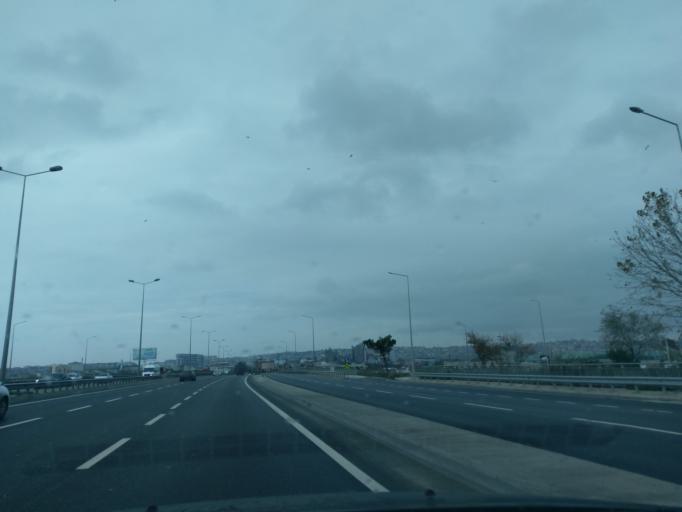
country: TR
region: Istanbul
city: Bueyuekcekmece
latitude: 41.0198
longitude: 28.5742
